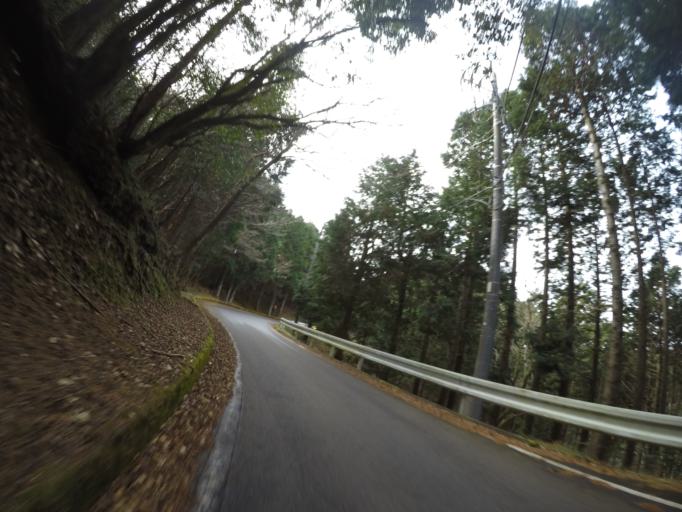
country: JP
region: Shizuoka
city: Heda
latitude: 34.8751
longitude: 138.8491
